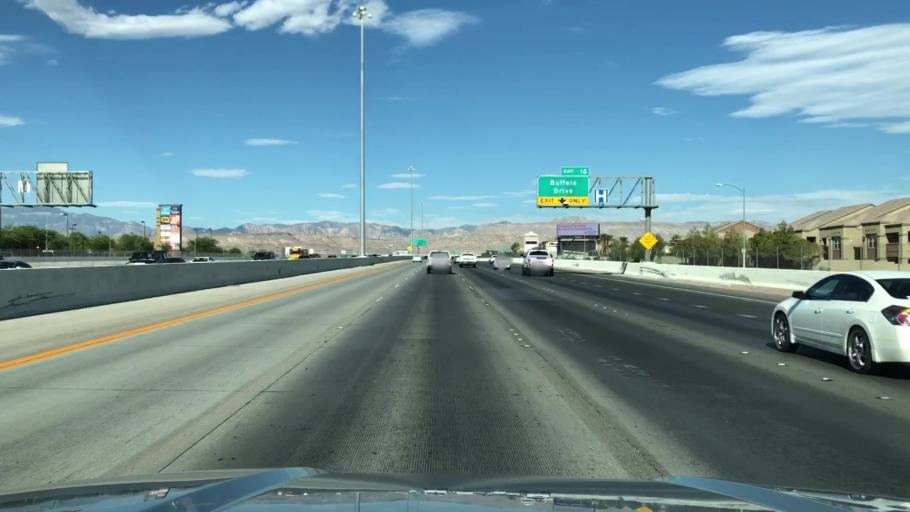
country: US
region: Nevada
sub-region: Clark County
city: Spring Valley
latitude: 36.0667
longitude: -115.2474
